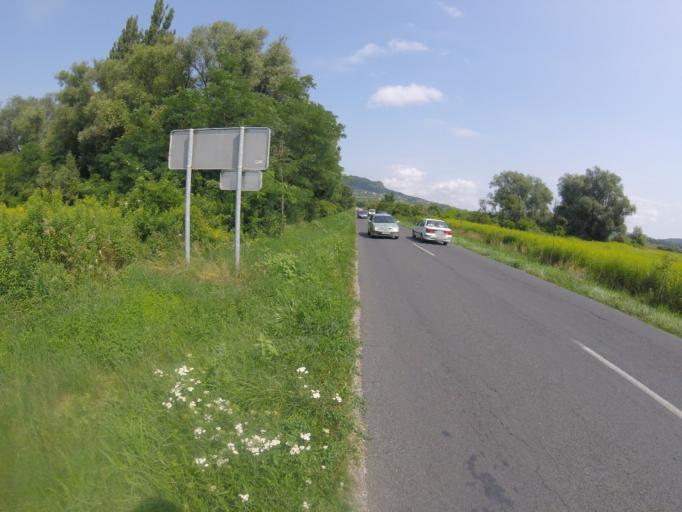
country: HU
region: Veszprem
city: Badacsonytomaj
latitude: 46.8142
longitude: 17.4477
